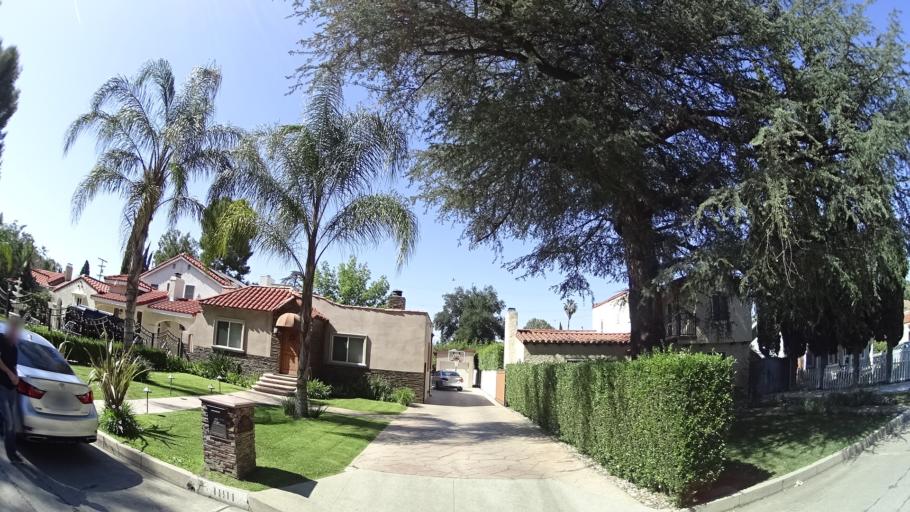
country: US
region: California
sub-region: Los Angeles County
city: North Hollywood
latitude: 34.1535
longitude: -118.3726
